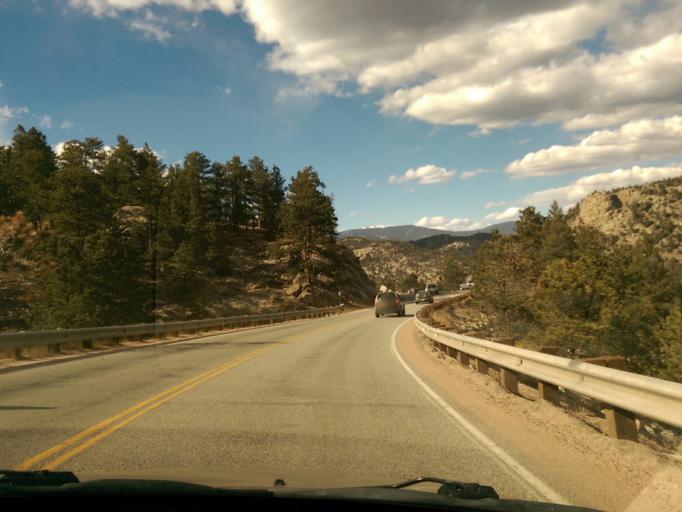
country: US
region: Colorado
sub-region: Larimer County
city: Estes Park
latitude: 40.3647
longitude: -105.4725
